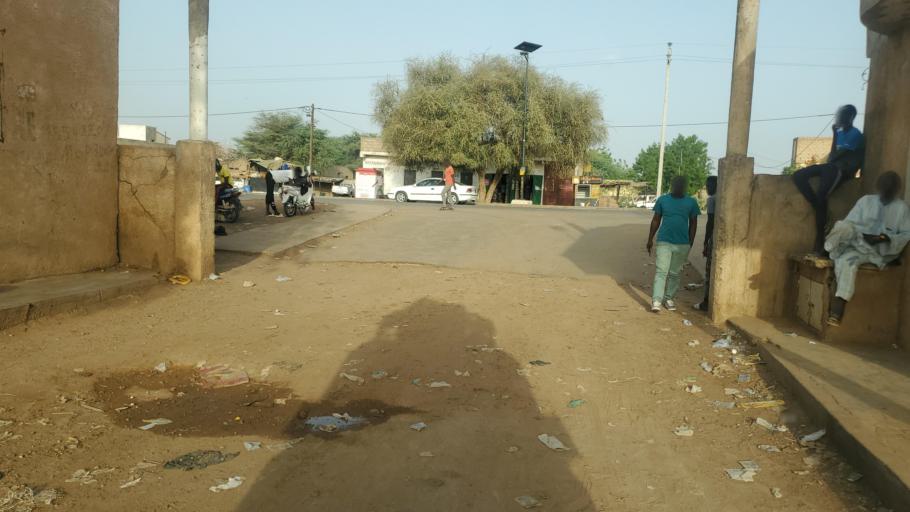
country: SN
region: Louga
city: Dara
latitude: 15.3486
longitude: -15.4895
